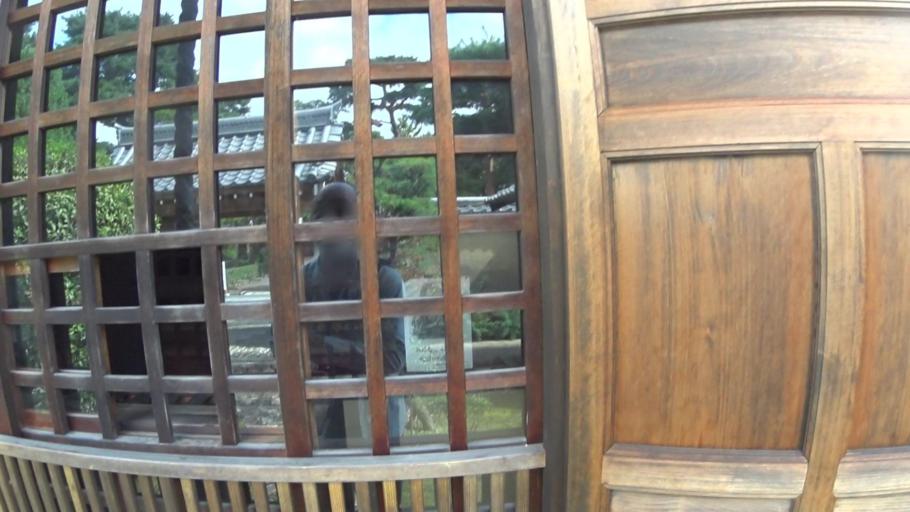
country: JP
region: Kyoto
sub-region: Kyoto-shi
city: Kamigyo-ku
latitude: 35.0337
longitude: 135.7613
